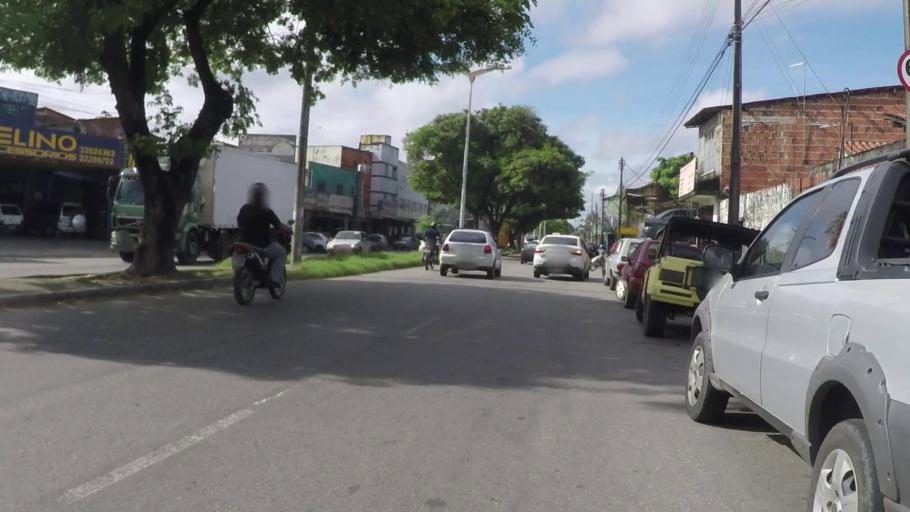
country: BR
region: Ceara
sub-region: Fortaleza
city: Fortaleza
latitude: -3.7196
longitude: -38.5875
